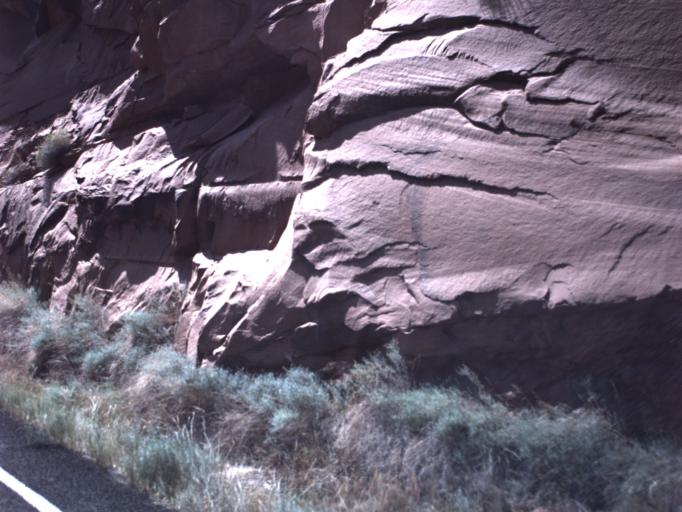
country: US
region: Utah
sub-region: Grand County
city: Moab
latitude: 38.5670
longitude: -109.5819
